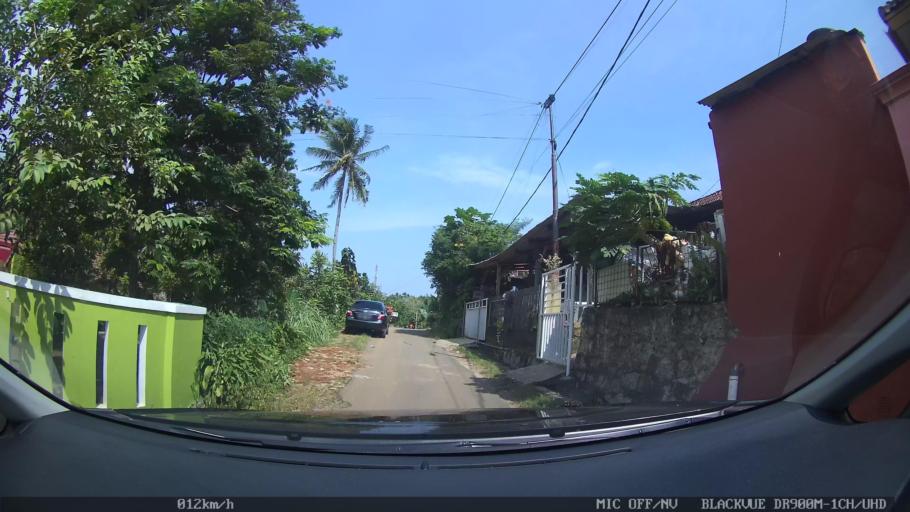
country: ID
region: Lampung
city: Kedaton
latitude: -5.4000
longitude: 105.2372
